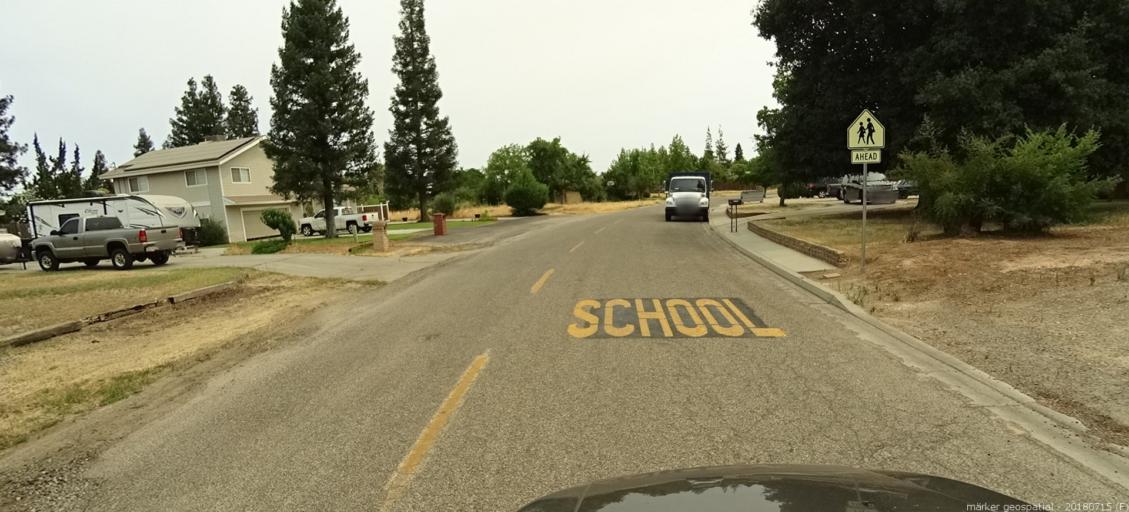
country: US
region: California
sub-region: Madera County
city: Madera Acres
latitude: 37.0228
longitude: -120.0610
